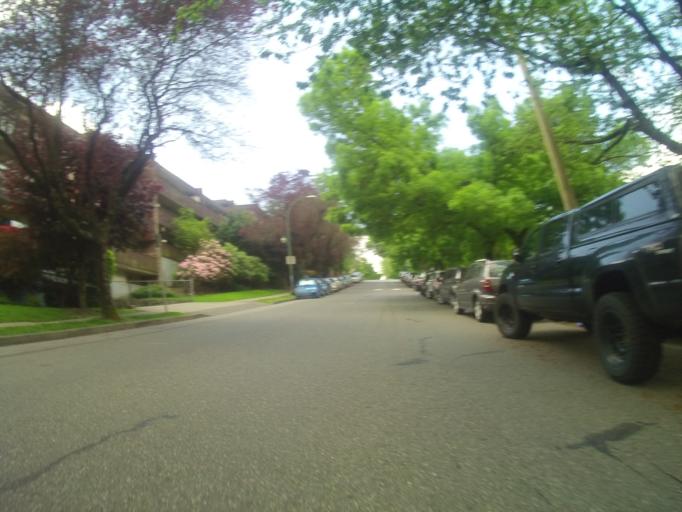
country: CA
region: British Columbia
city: Vancouver
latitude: 49.2643
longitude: -123.0837
